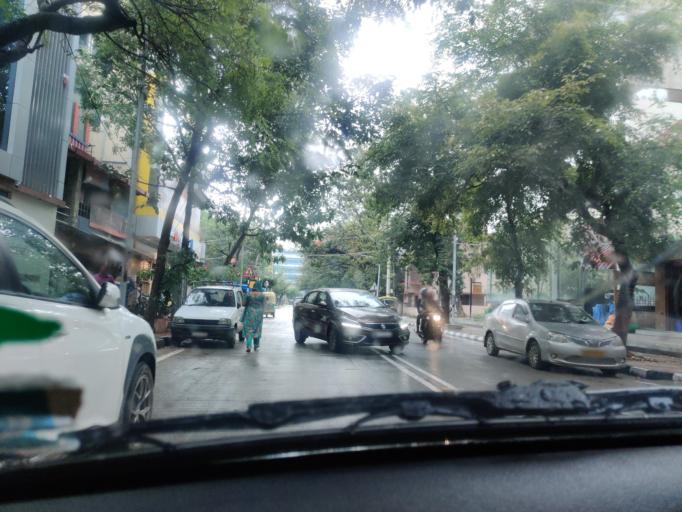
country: IN
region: Karnataka
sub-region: Bangalore Urban
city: Bangalore
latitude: 13.0241
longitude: 77.6331
